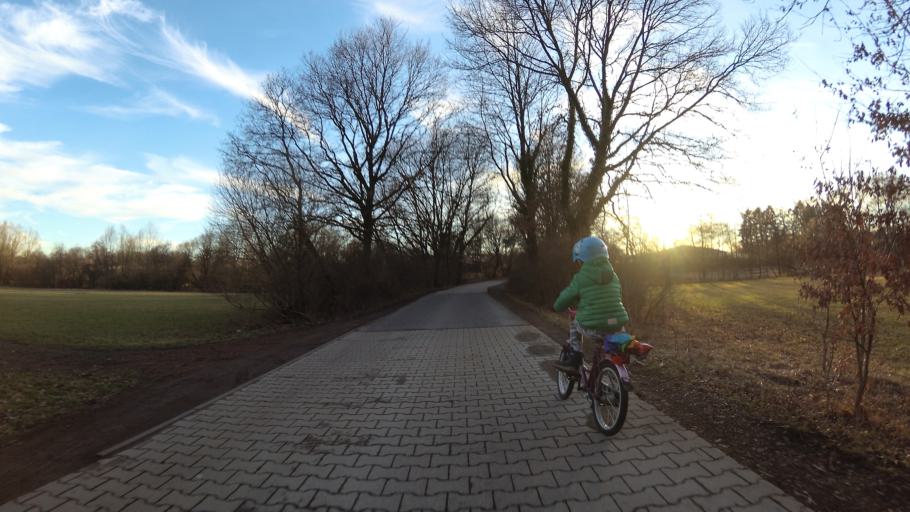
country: DE
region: Saarland
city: Namborn
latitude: 49.4912
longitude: 7.1275
